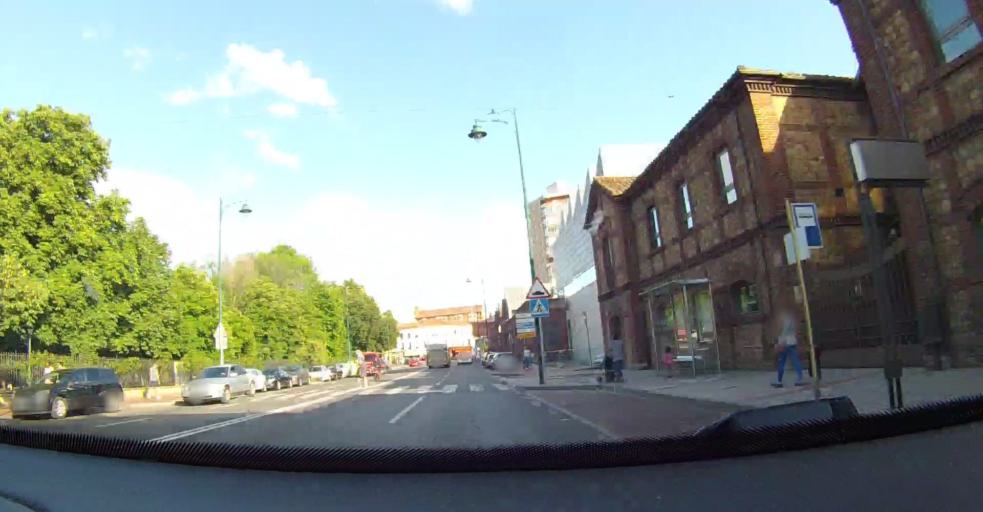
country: ES
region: Castille and Leon
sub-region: Provincia de Leon
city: Leon
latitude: 42.6013
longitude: -5.5871
